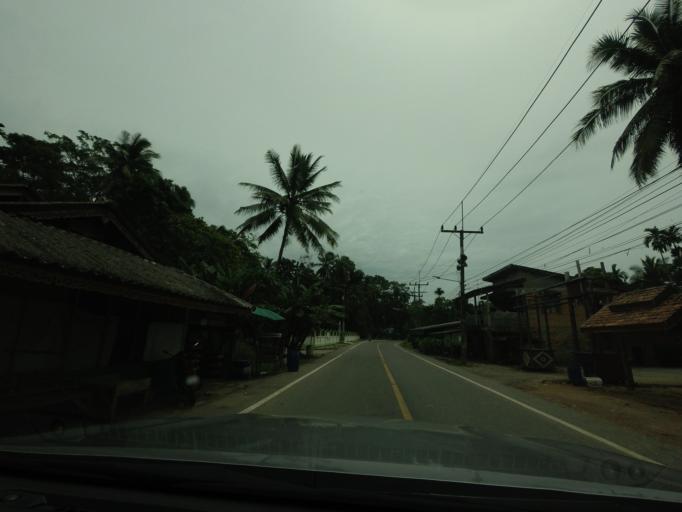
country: TH
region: Pattani
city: Kapho
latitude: 6.6424
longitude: 101.5502
